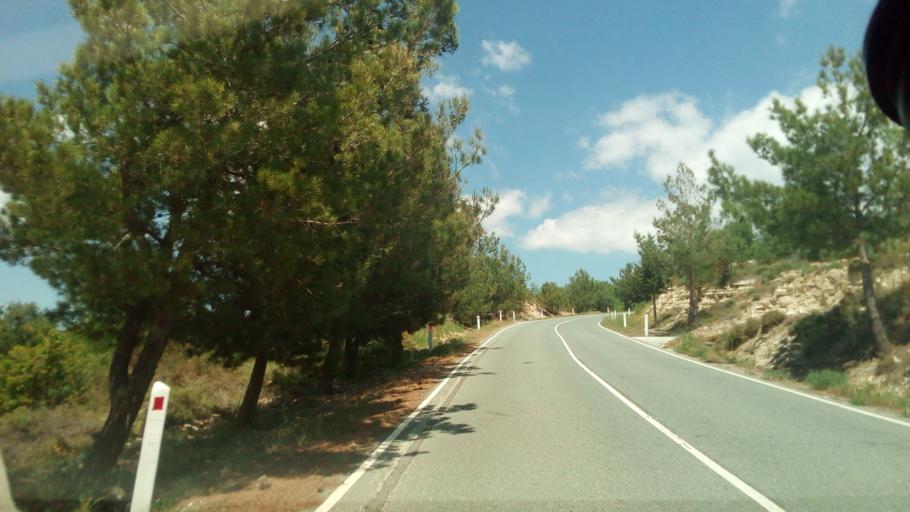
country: CY
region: Limassol
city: Pachna
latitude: 34.8298
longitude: 32.7708
